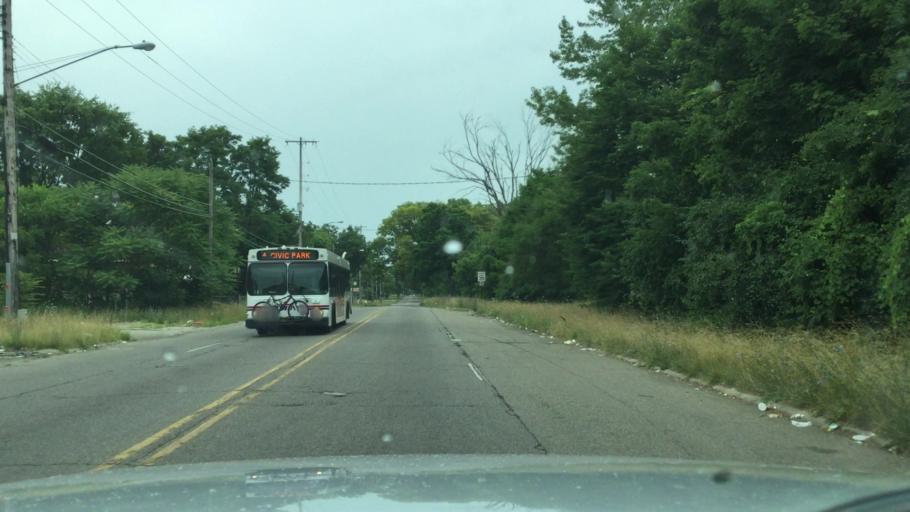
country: US
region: Michigan
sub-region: Genesee County
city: Beecher
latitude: 43.0604
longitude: -83.7237
